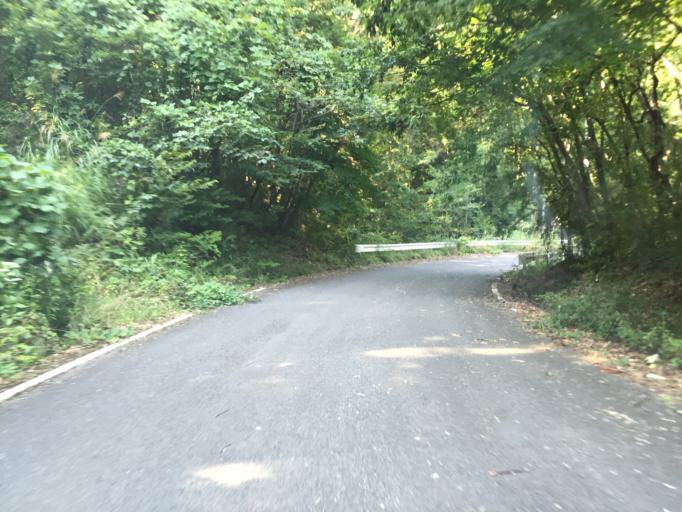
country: JP
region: Fukushima
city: Nihommatsu
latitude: 37.6087
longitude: 140.3847
